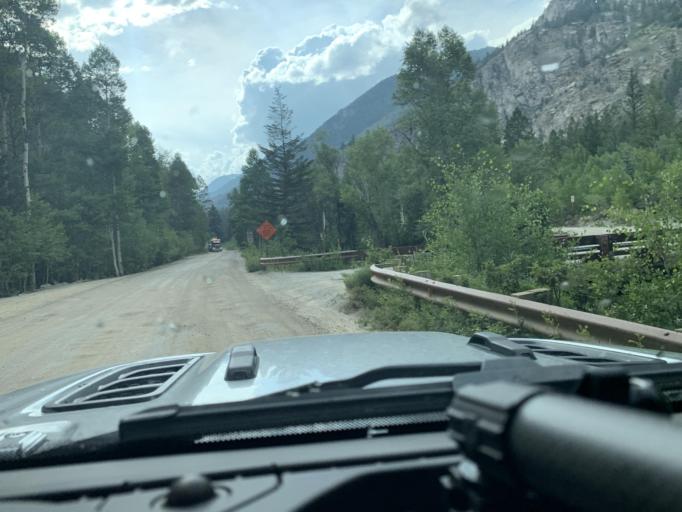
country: US
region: Colorado
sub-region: Chaffee County
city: Buena Vista
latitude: 38.7156
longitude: -106.2554
